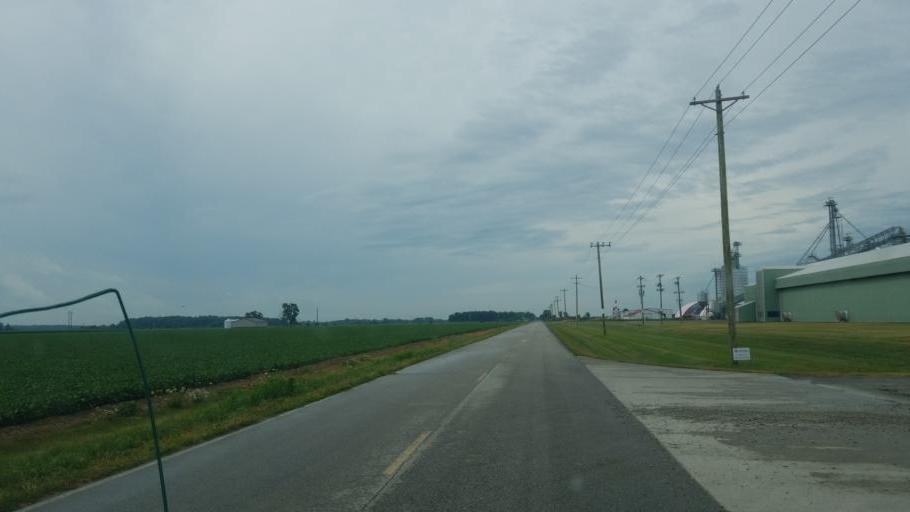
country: US
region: Ohio
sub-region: Defiance County
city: Hicksville
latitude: 41.3024
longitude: -84.6897
